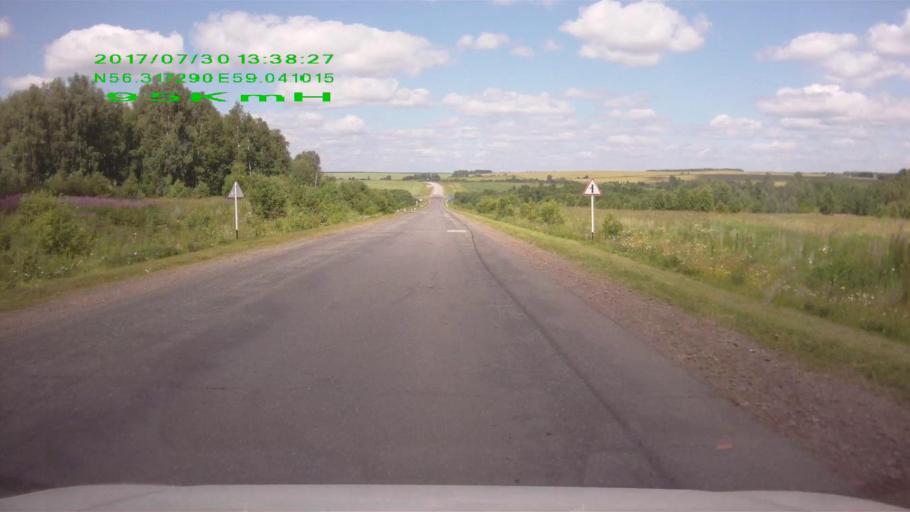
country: RU
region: Sverdlovsk
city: Mikhaylovsk
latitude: 56.3179
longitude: 59.0411
